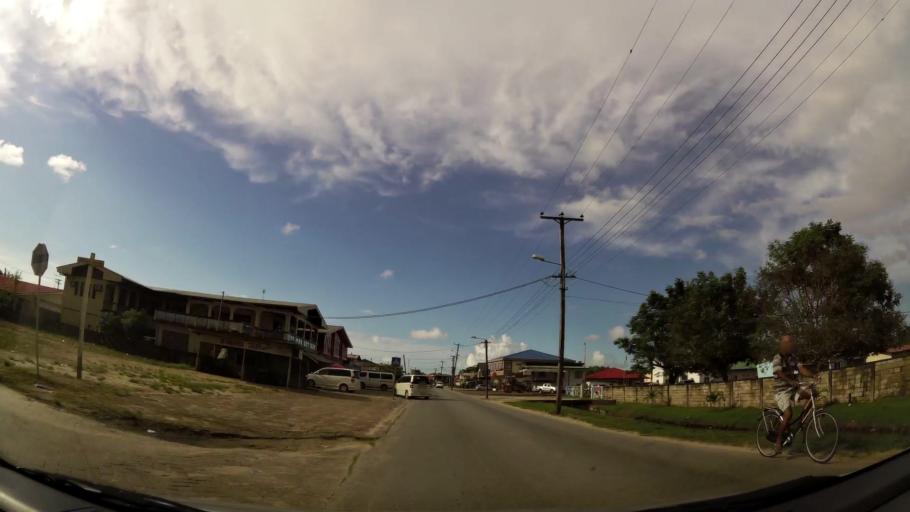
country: SR
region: Paramaribo
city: Paramaribo
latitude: 5.8428
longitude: -55.1815
